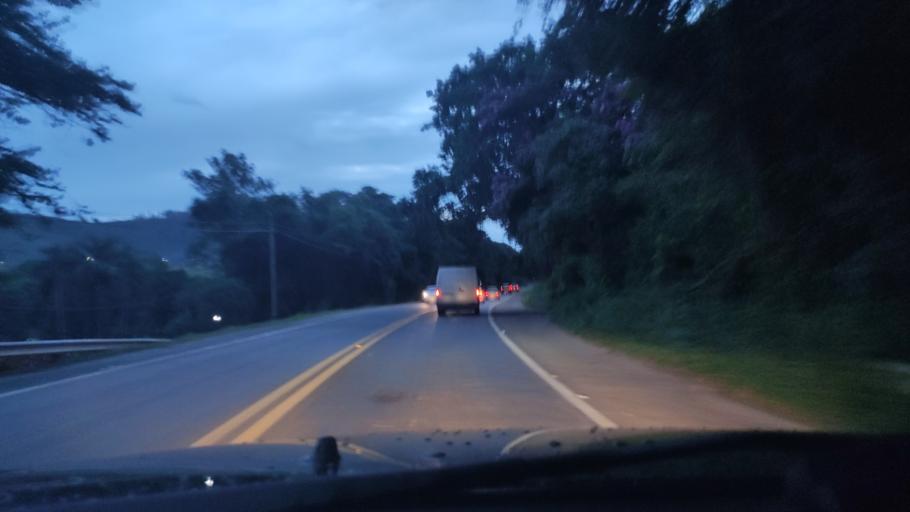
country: BR
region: Sao Paulo
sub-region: Socorro
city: Socorro
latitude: -22.6291
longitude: -46.5342
